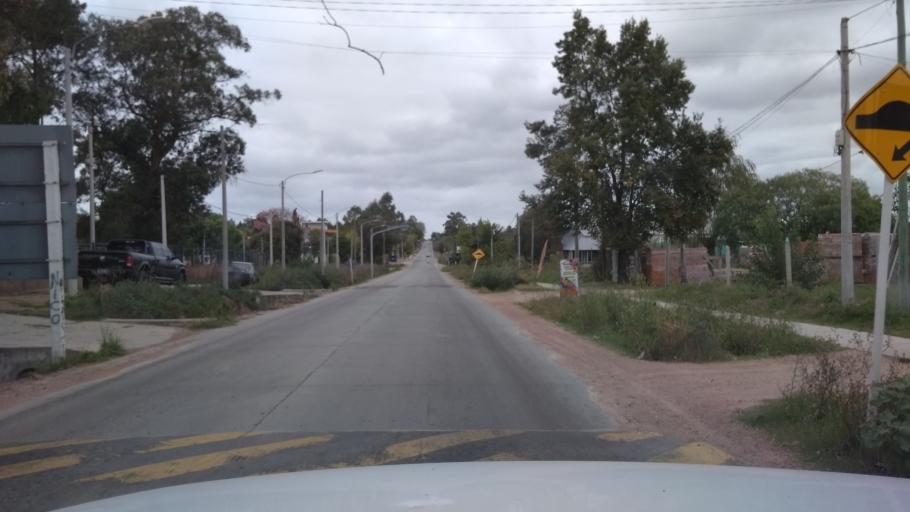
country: UY
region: Canelones
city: Toledo
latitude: -34.7823
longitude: -56.1375
